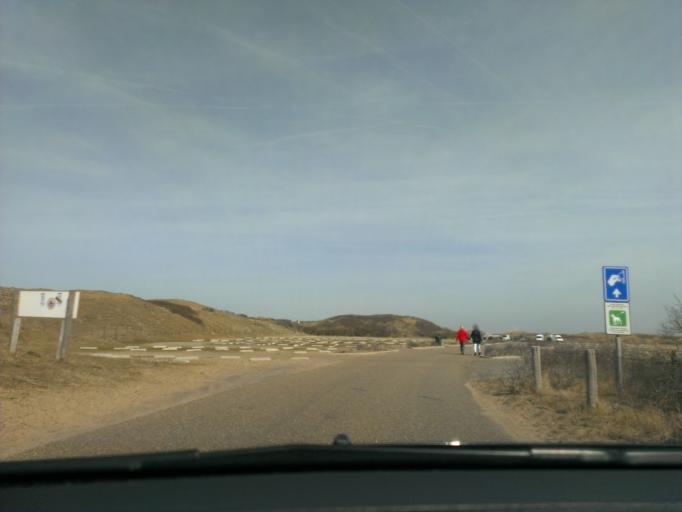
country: NL
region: North Holland
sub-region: Gemeente Zandvoort
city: Zandvoort
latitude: 52.4150
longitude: 4.5533
